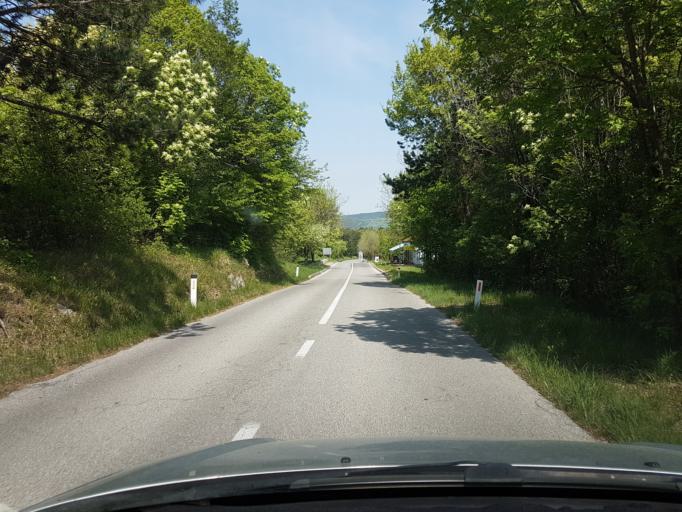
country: IT
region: Friuli Venezia Giulia
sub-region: Provincia di Trieste
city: Aurisina
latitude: 45.7804
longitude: 13.7005
